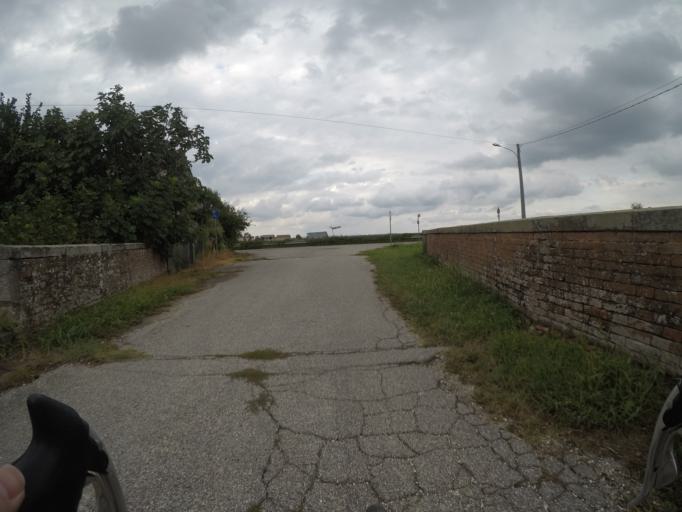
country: IT
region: Veneto
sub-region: Provincia di Rovigo
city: Polesella
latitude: 44.9612
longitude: 11.7299
